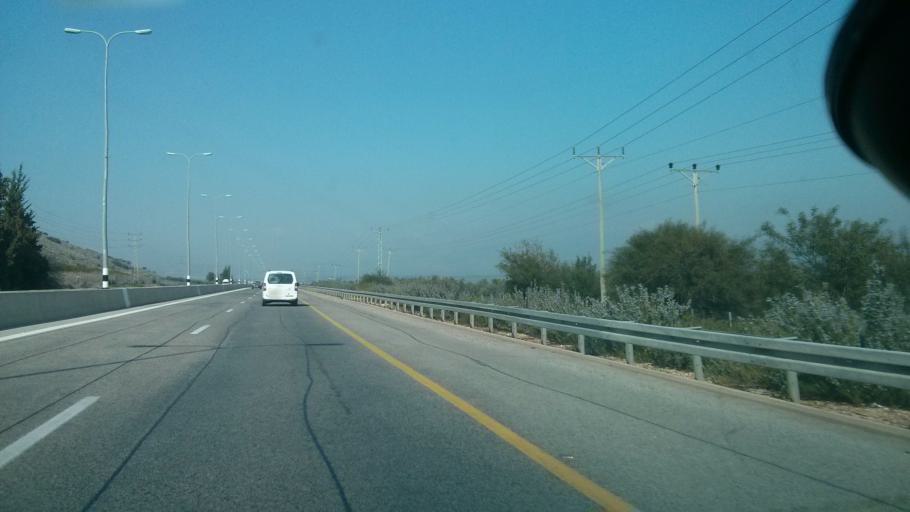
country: IL
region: Northern District
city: Rosh Pinna
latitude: 33.0647
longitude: 35.5752
